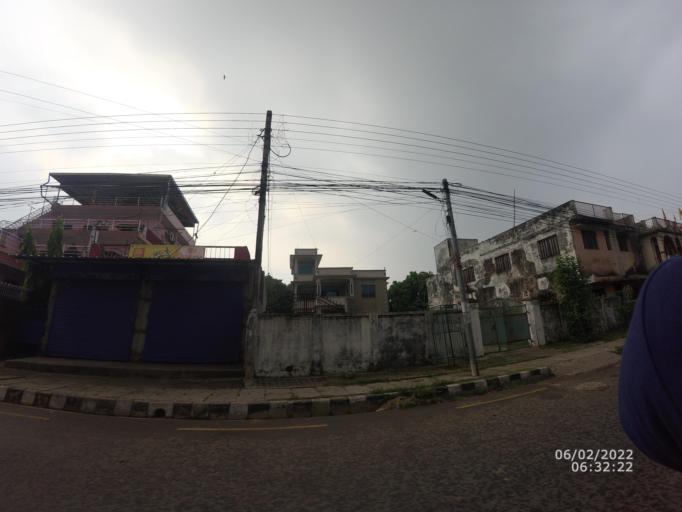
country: NP
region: Western Region
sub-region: Lumbini Zone
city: Bhairahawa
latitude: 27.5003
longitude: 83.4487
